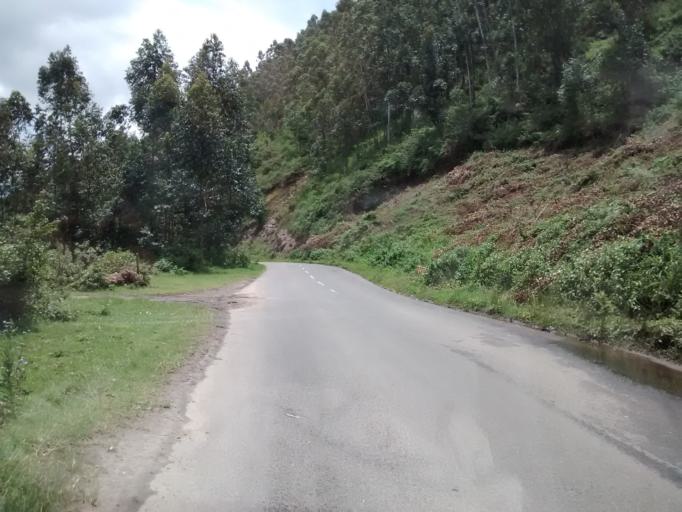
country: IN
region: Kerala
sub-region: Idukki
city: Munnar
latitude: 10.1248
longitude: 77.1615
